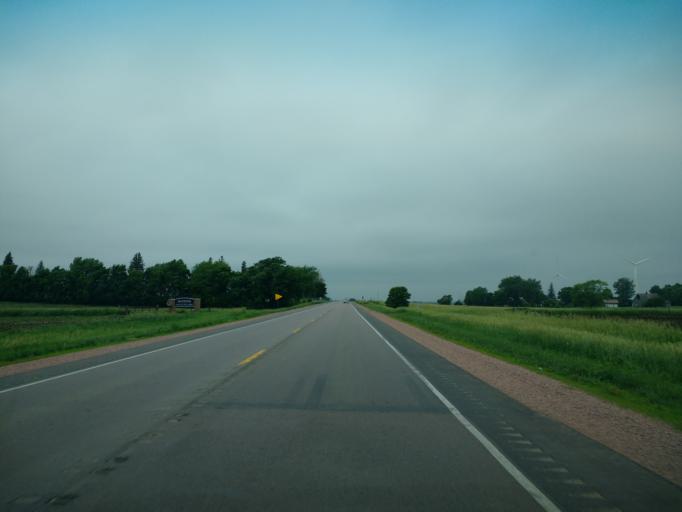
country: US
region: Iowa
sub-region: O'Brien County
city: Sanborn
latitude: 43.1861
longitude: -95.6777
